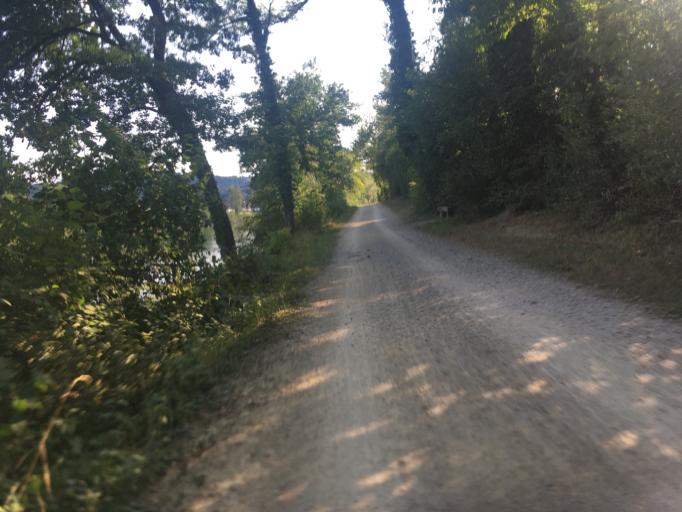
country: CH
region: Bern
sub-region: Biel/Bienne District
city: Orpund
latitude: 47.1284
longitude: 7.2983
